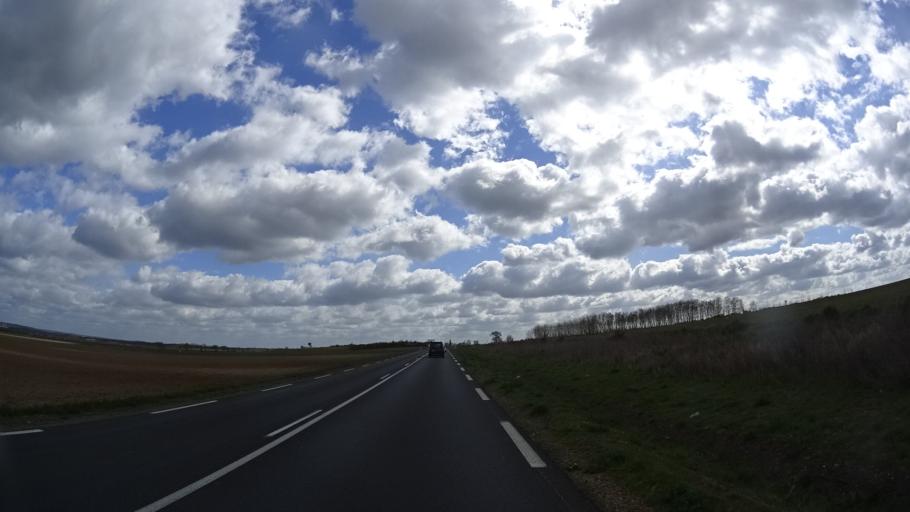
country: FR
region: Pays de la Loire
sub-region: Departement de Maine-et-Loire
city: Breze
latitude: 47.0879
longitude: -0.0560
